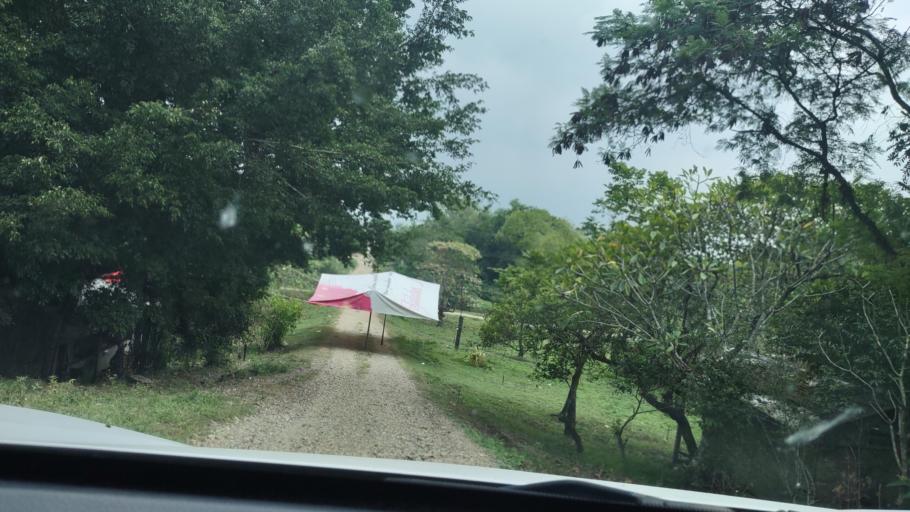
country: MX
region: Veracruz
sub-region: Uxpanapa
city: Poblado 10
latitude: 17.5490
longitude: -94.2930
